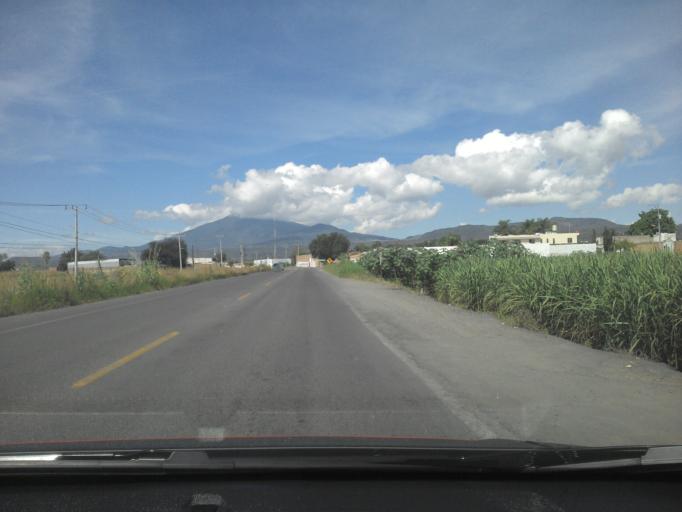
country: MX
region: Jalisco
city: El Refugio
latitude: 20.6642
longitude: -103.7368
